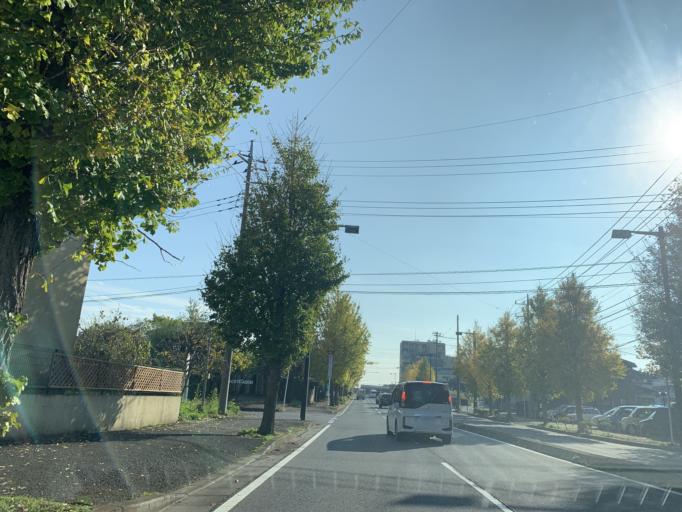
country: JP
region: Chiba
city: Nagareyama
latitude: 35.8608
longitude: 139.9122
